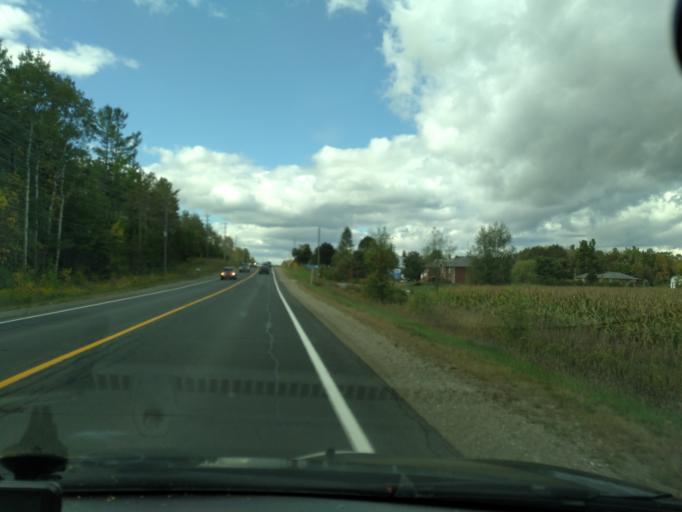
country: CA
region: Ontario
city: Angus
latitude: 44.2544
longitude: -79.7959
